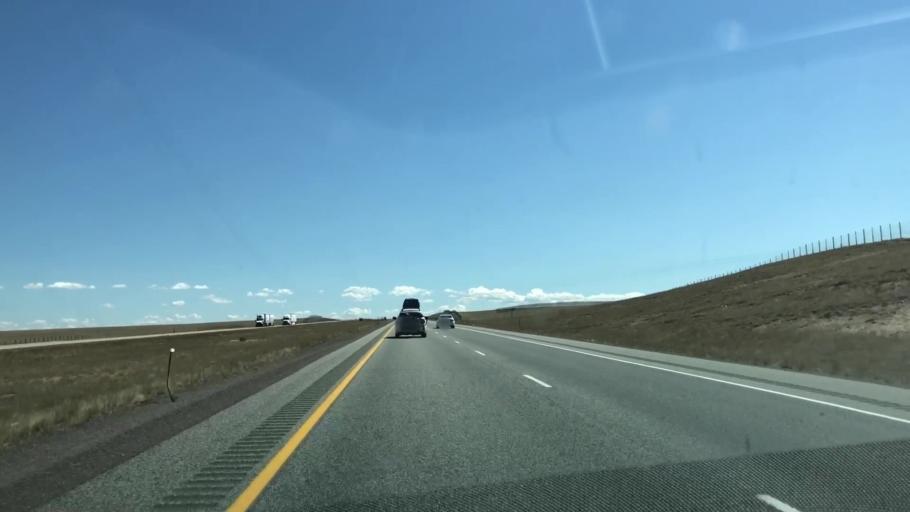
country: US
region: Wyoming
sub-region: Albany County
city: Laramie
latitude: 41.4764
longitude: -106.0101
